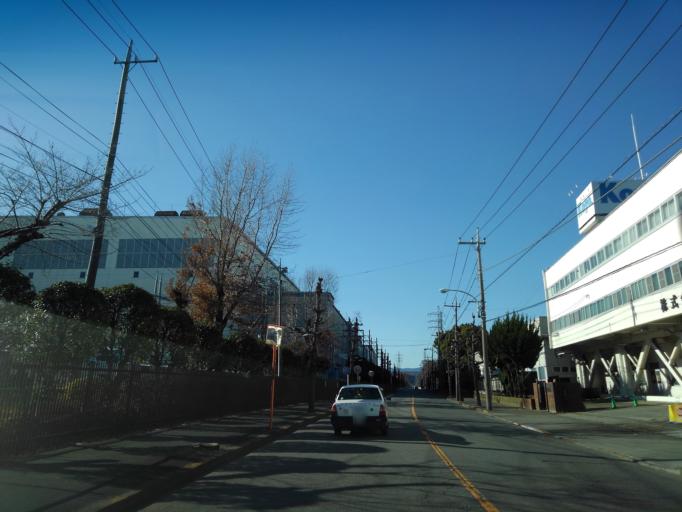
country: JP
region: Tokyo
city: Fussa
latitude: 35.7756
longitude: 139.3189
